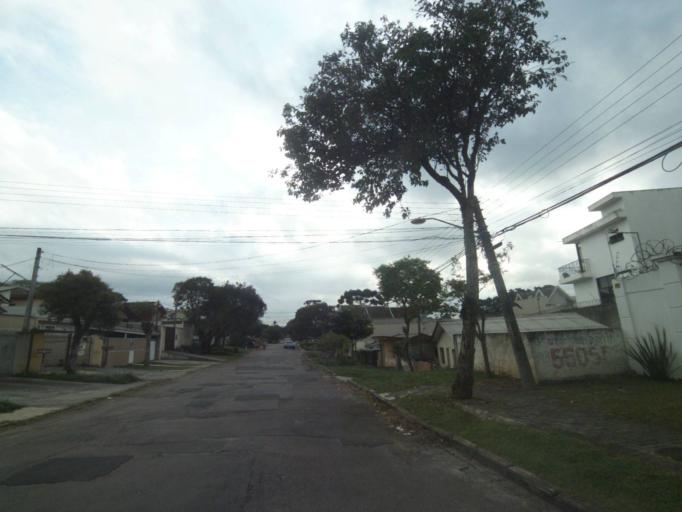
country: BR
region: Parana
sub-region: Pinhais
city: Pinhais
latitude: -25.4126
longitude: -49.2114
